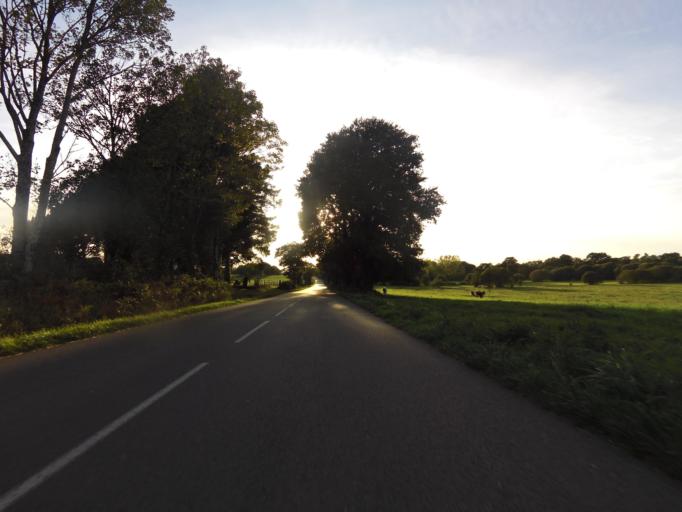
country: FR
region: Brittany
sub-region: Departement du Morbihan
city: Theix
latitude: 47.6338
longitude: -2.6299
